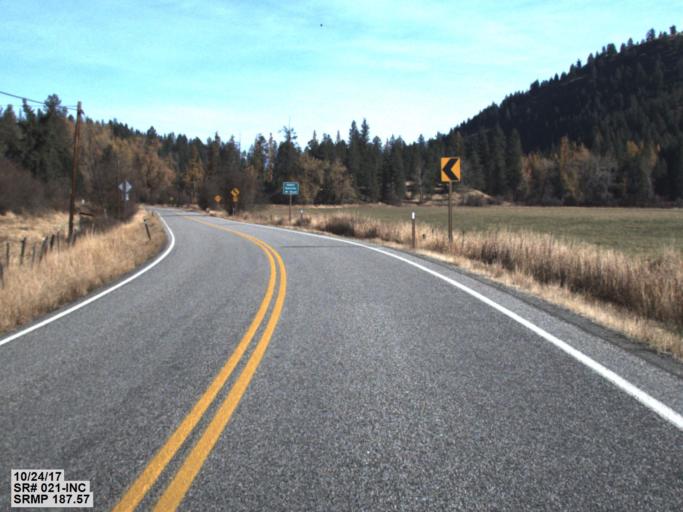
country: CA
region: British Columbia
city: Grand Forks
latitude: 48.9567
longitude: -118.5358
